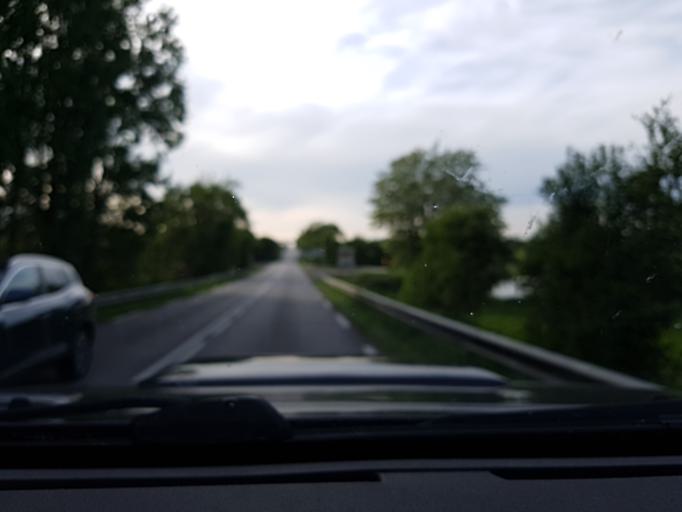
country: FR
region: Pays de la Loire
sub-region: Departement de la Vendee
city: Mache
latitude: 46.7692
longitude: -1.6644
